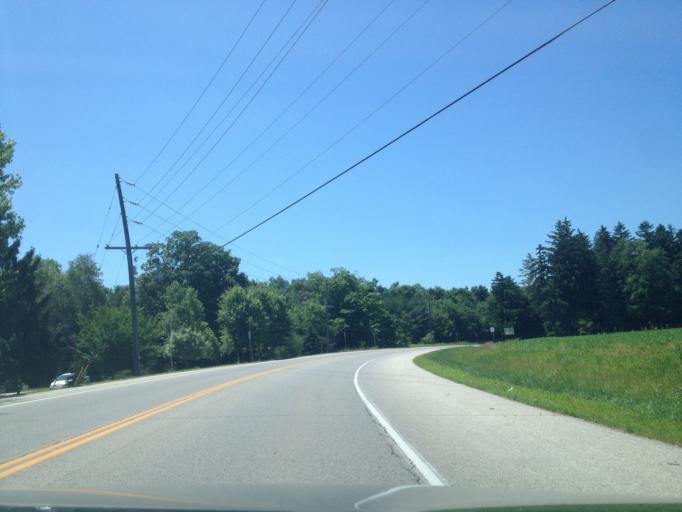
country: CA
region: Ontario
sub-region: Wellington County
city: Guelph
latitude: 43.6910
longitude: -80.3927
